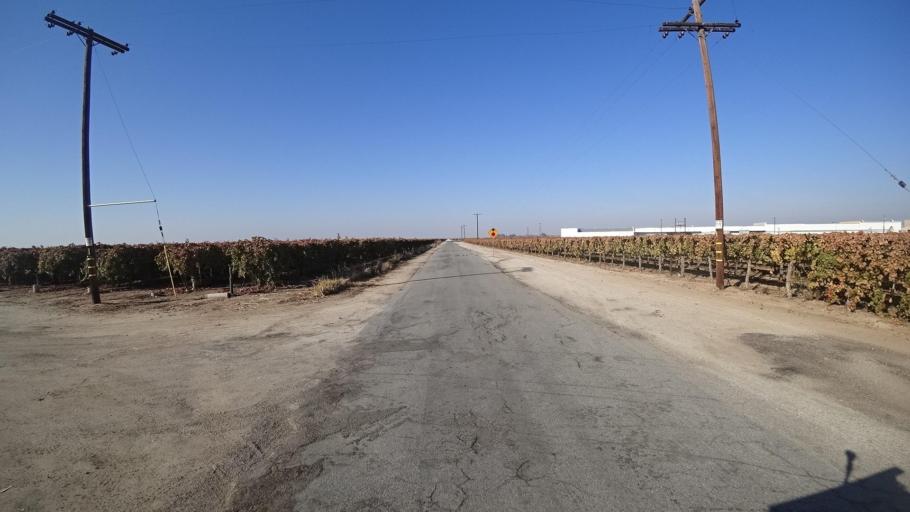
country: US
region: California
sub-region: Tulare County
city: Richgrove
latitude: 35.7398
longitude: -119.1431
